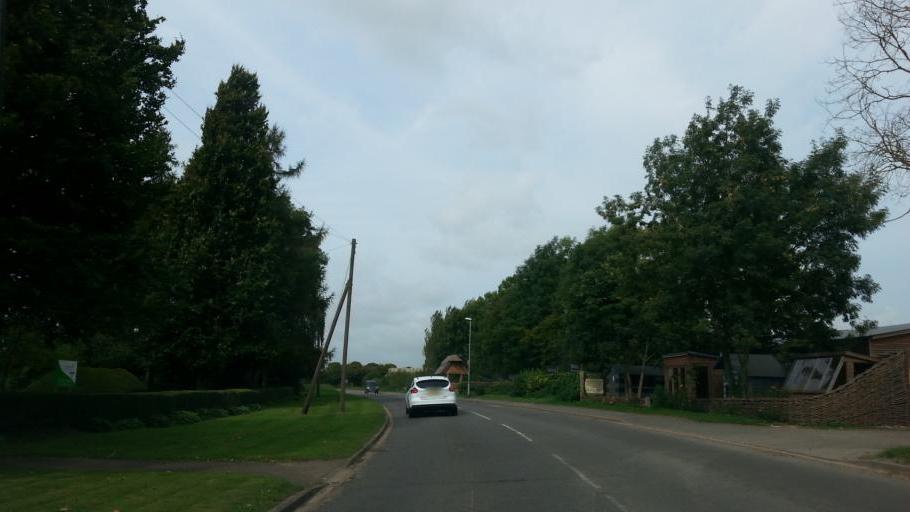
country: GB
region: England
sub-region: Cambridgeshire
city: Barton
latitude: 52.1849
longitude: 0.0509
